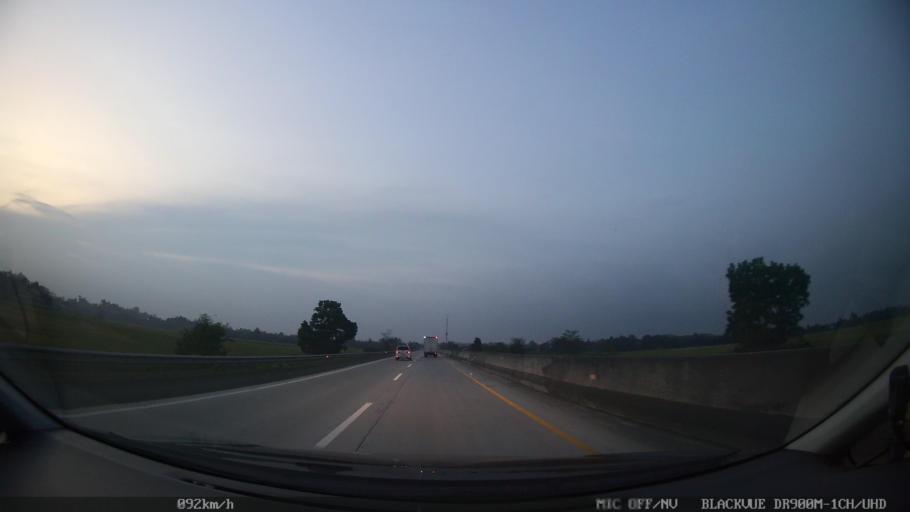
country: ID
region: Lampung
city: Sidorejo
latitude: -5.5779
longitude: 105.5413
